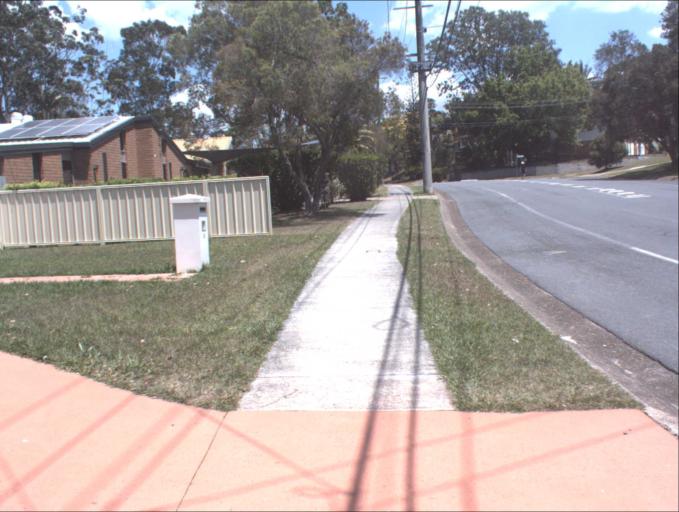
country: AU
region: Queensland
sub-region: Logan
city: Springwood
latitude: -27.5998
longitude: 153.1409
